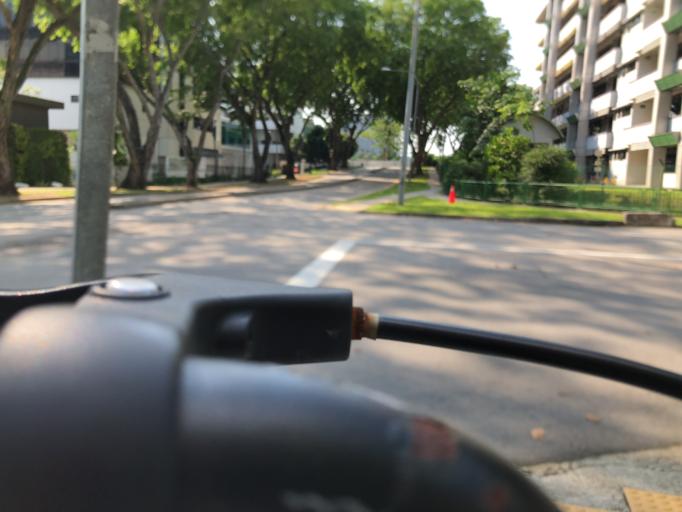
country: SG
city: Singapore
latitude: 1.2944
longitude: 103.7876
